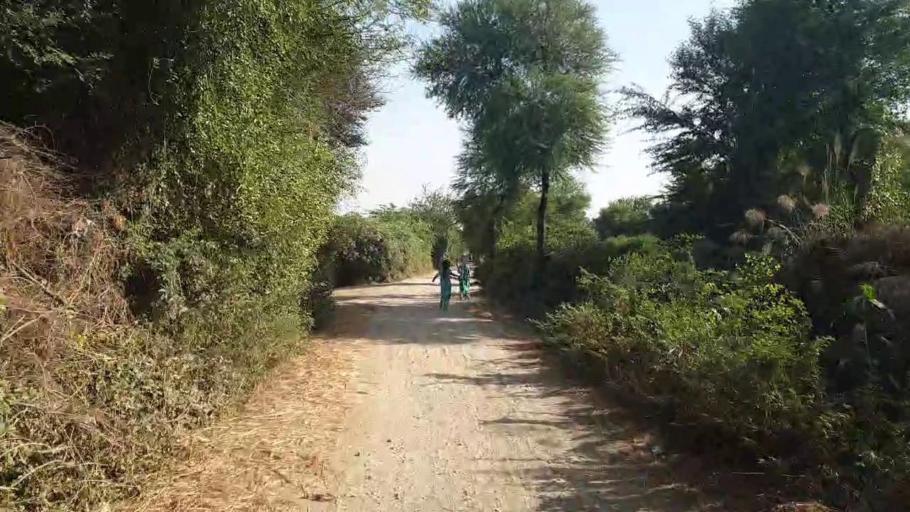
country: PK
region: Sindh
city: Matli
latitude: 25.0262
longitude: 68.7336
